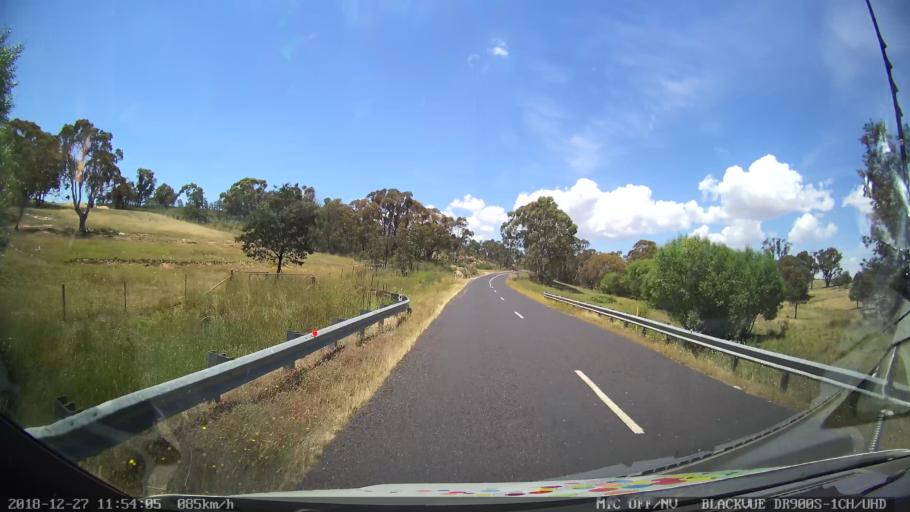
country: AU
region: New South Wales
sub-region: Blayney
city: Blayney
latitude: -33.6704
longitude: 149.4018
